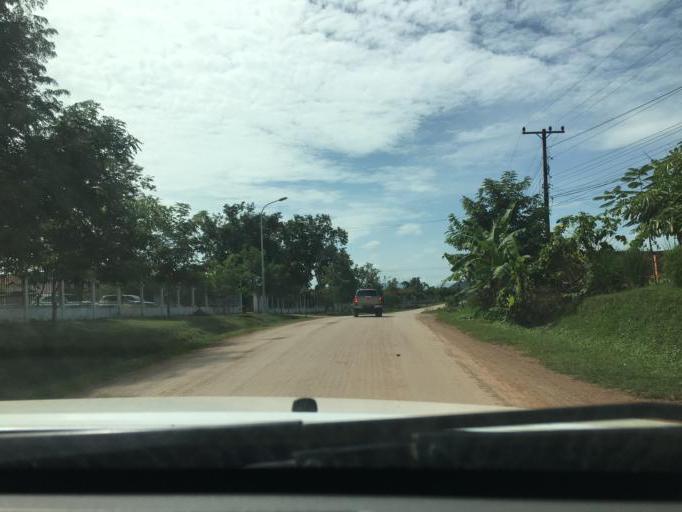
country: LA
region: Xiagnabouli
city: Muang Kenthao
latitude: 17.7127
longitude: 101.4068
